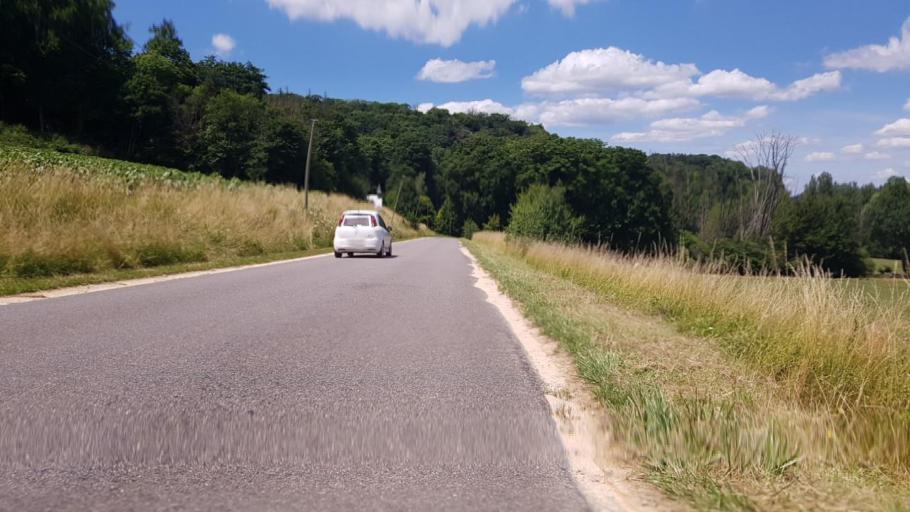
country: FR
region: Lorraine
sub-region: Departement de la Meuse
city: Gondrecourt-le-Chateau
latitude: 48.6324
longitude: 5.4564
